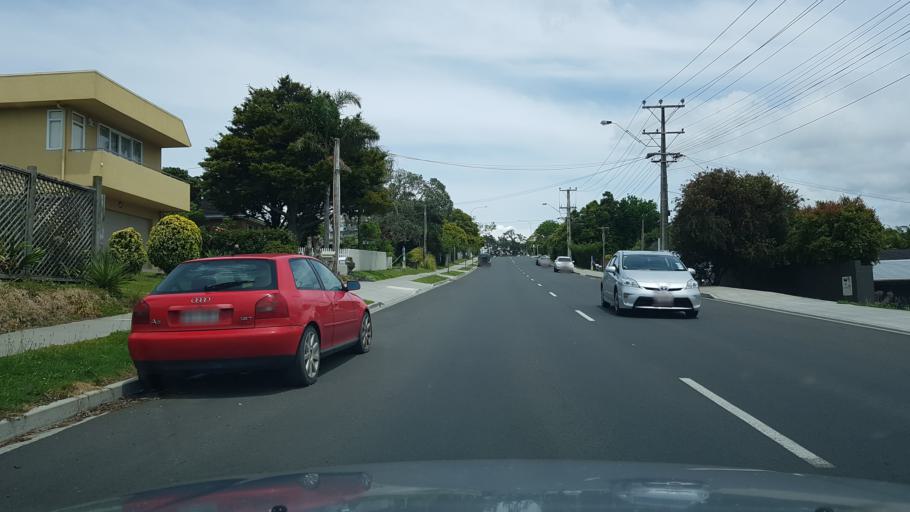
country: NZ
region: Auckland
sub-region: Auckland
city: North Shore
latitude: -36.8029
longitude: 174.7285
